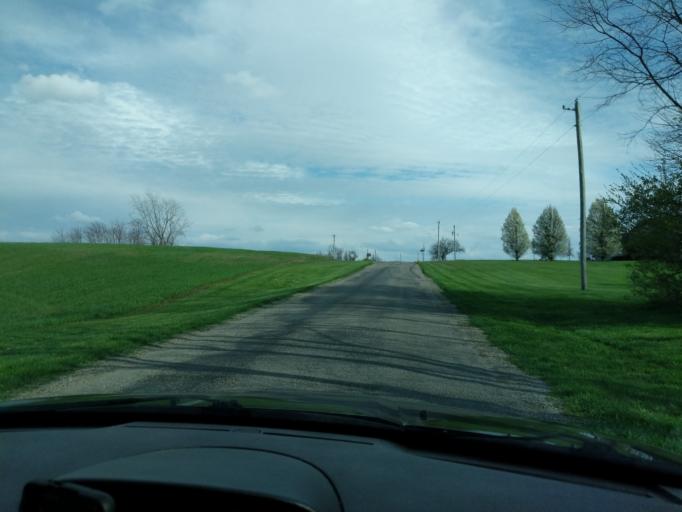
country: US
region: Ohio
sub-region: Logan County
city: West Liberty
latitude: 40.2006
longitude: -83.6631
